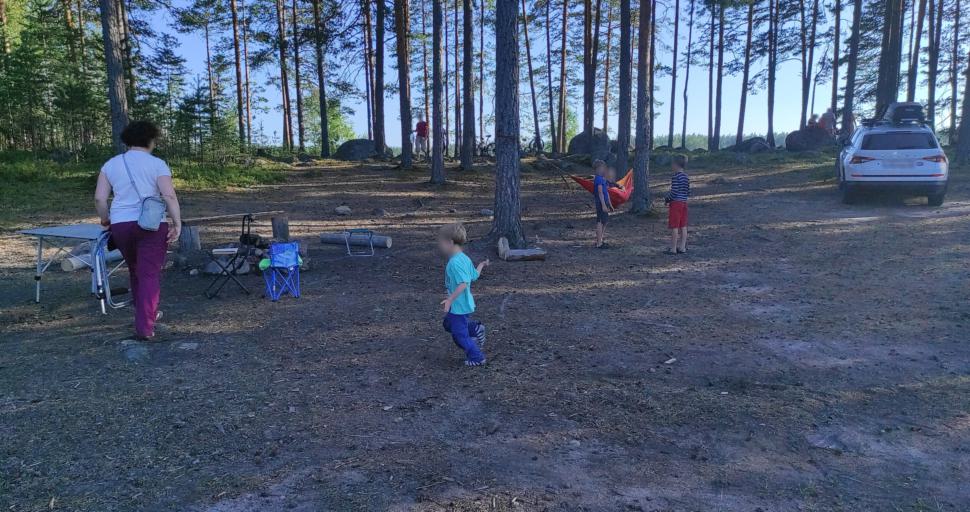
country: RU
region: Leningrad
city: Veshchevo
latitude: 60.6820
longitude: 29.2673
